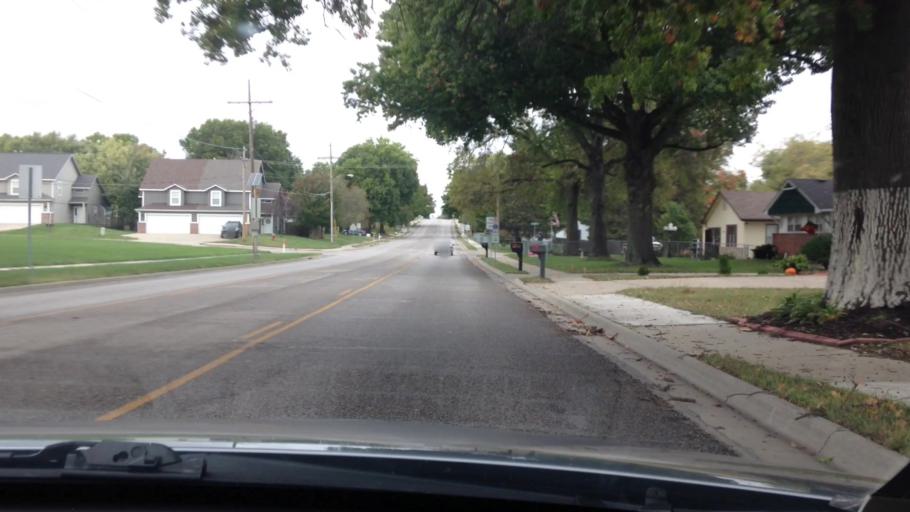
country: US
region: Kansas
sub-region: Leavenworth County
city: Leavenworth
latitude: 39.2968
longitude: -94.9276
